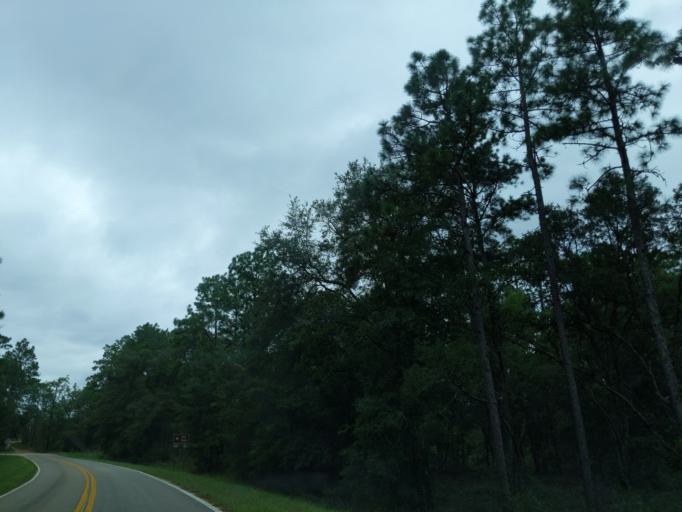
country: US
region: Florida
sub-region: Gadsden County
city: Midway
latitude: 30.4025
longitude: -84.4129
